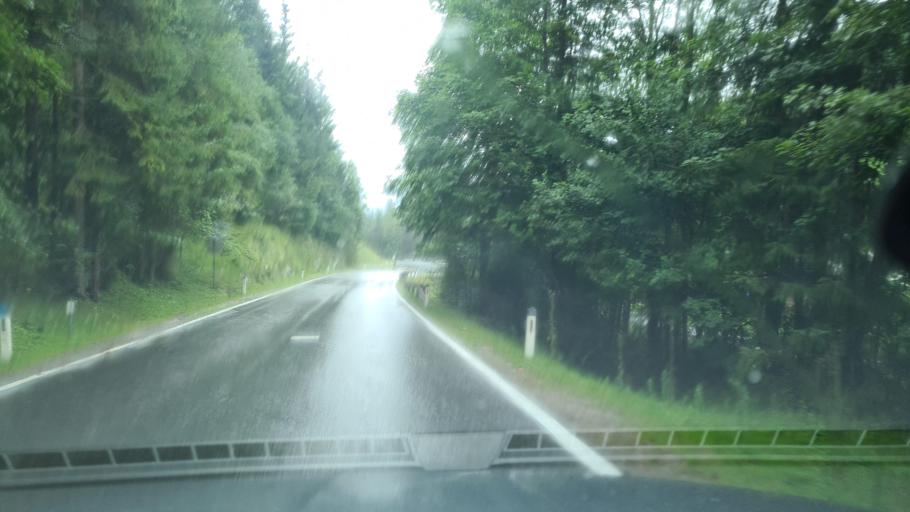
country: AT
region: Salzburg
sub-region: Politischer Bezirk Sankt Johann im Pongau
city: Altenmarkt im Pongau
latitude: 47.3523
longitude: 13.4291
